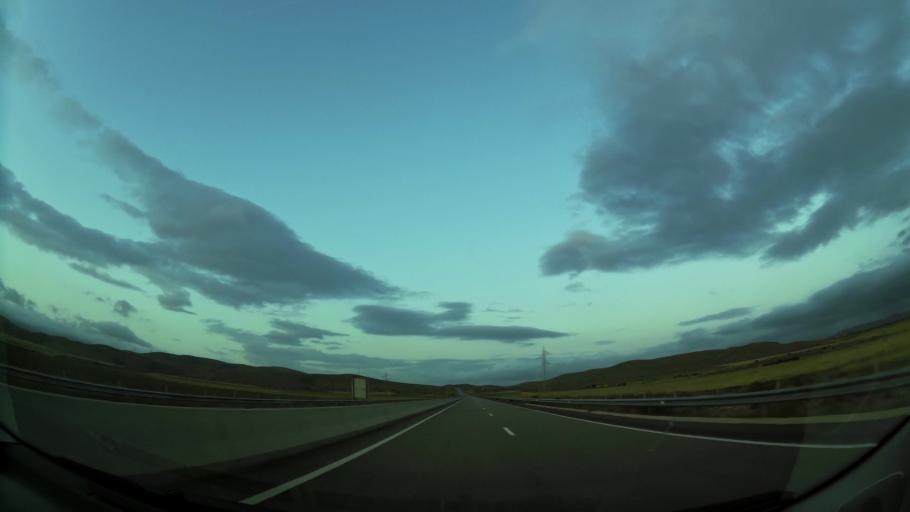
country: MA
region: Oriental
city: El Aioun
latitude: 34.6050
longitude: -2.6078
